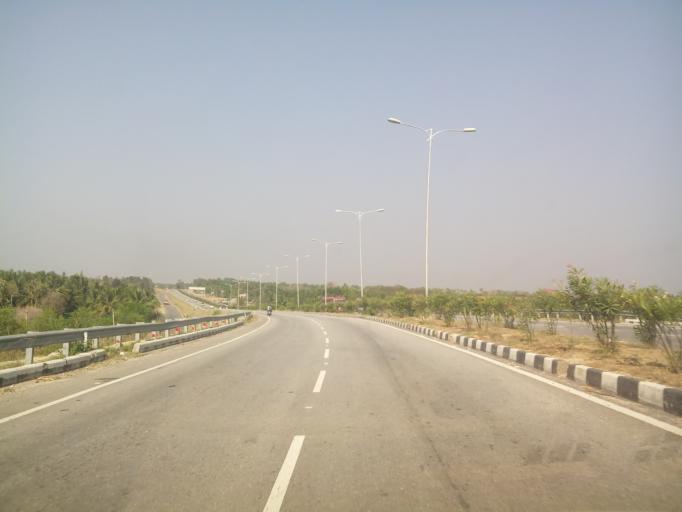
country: IN
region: Karnataka
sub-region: Tumkur
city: Kunigal
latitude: 13.0034
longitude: 76.9548
